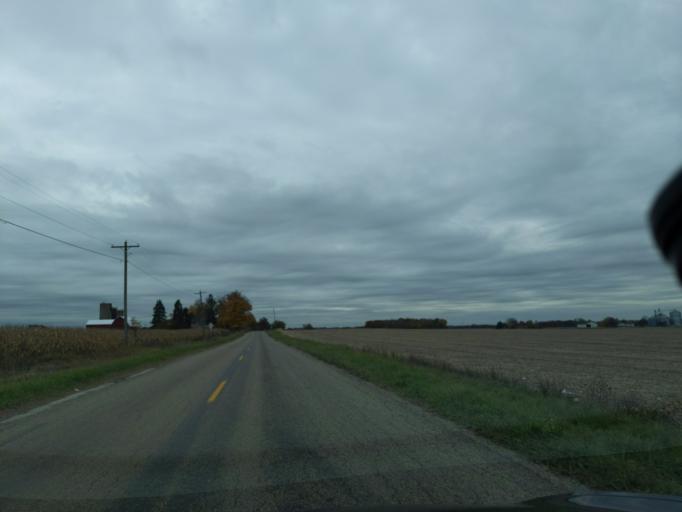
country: US
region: Michigan
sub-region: Eaton County
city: Eaton Rapids
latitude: 42.4430
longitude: -84.6006
